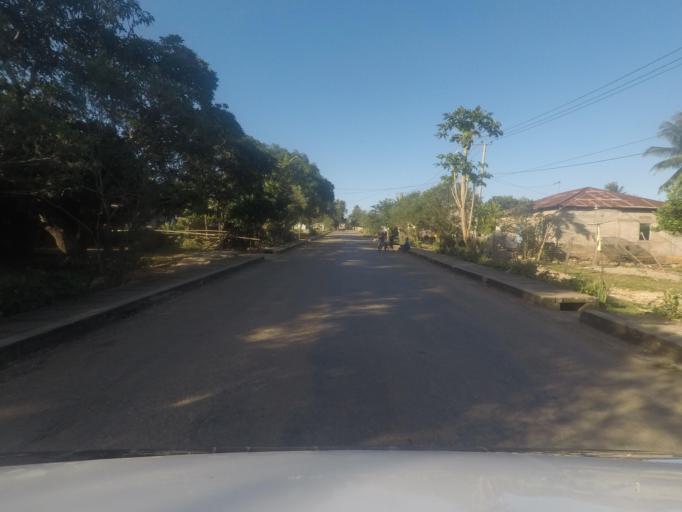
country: TL
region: Lautem
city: Lospalos
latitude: -8.4014
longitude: 127.1818
